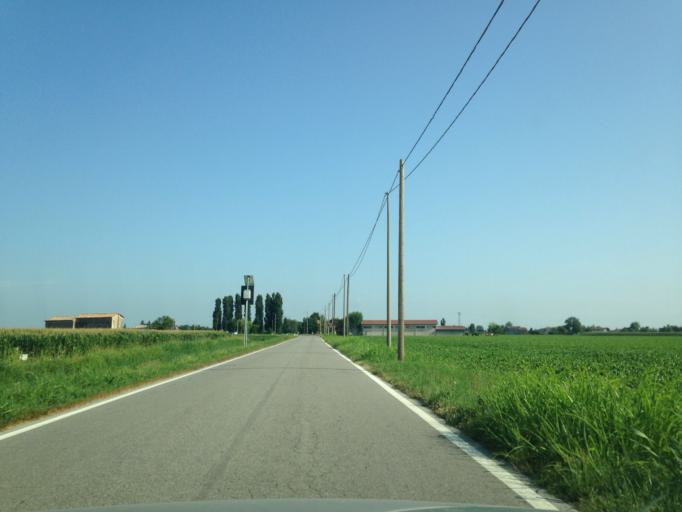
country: IT
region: Veneto
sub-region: Provincia di Venezia
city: Lugugnana
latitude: 45.7258
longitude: 12.9352
